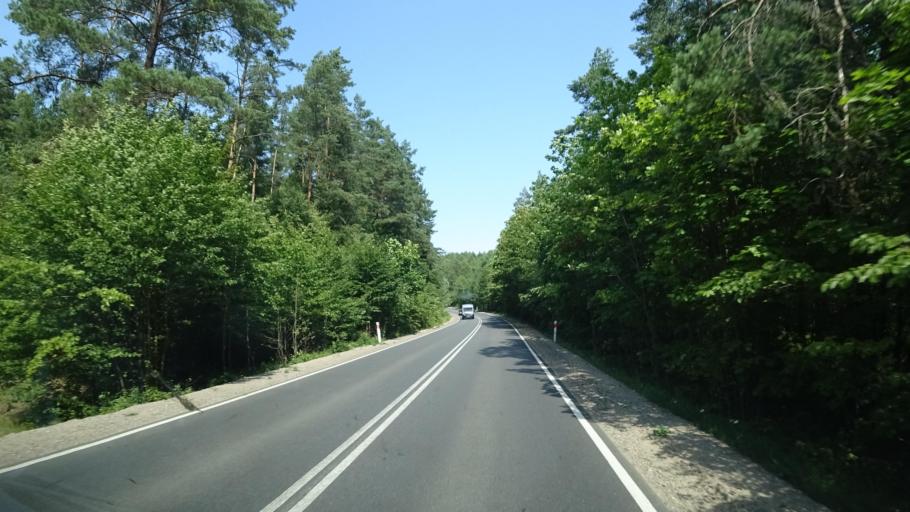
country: PL
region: Pomeranian Voivodeship
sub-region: Powiat koscierski
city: Dziemiany
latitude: 53.9814
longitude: 17.7739
